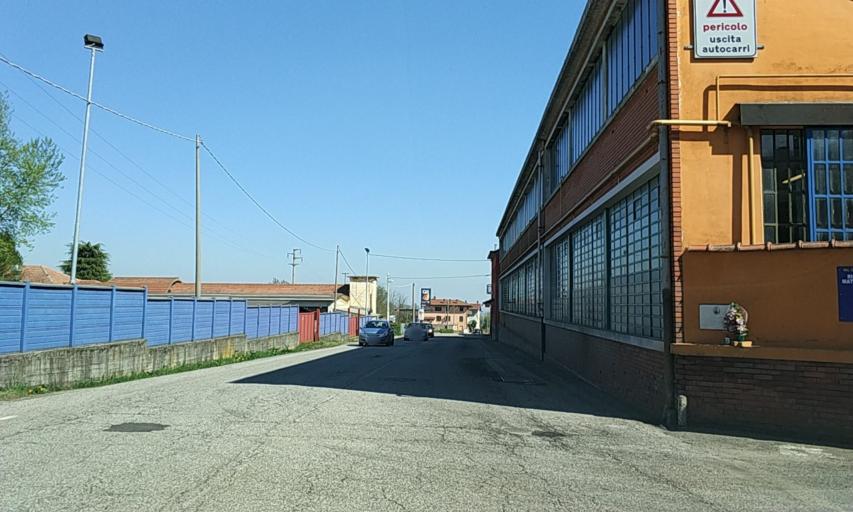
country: IT
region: Piedmont
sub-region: Provincia di Torino
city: Levone
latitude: 45.3367
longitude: 7.6096
